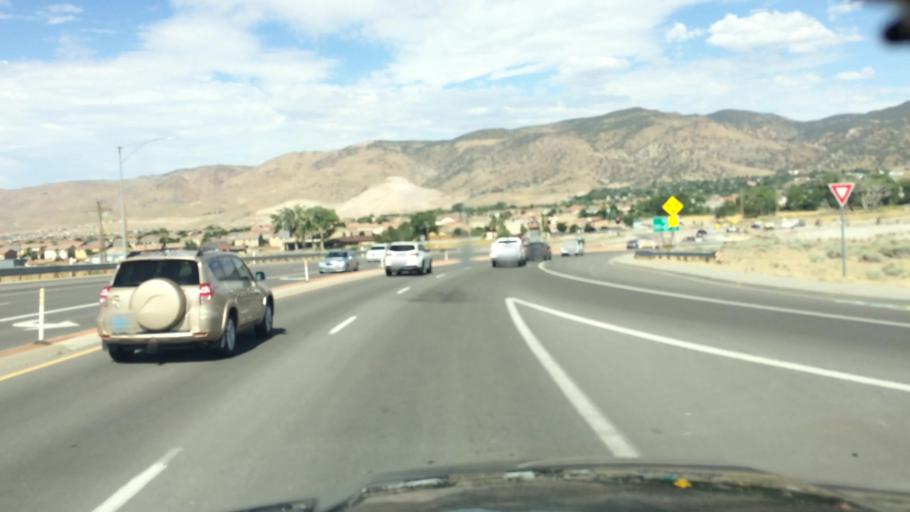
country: US
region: Nevada
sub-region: Washoe County
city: Sparks
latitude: 39.4030
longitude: -119.7456
